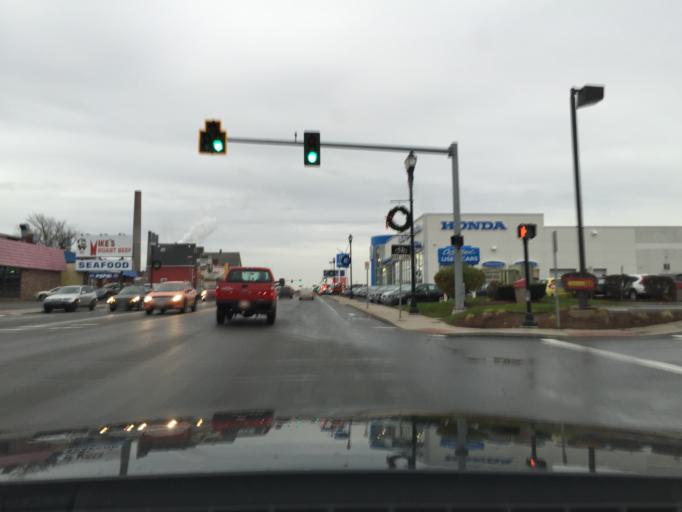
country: US
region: Massachusetts
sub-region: Middlesex County
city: Everett
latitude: 42.3984
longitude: -71.0637
